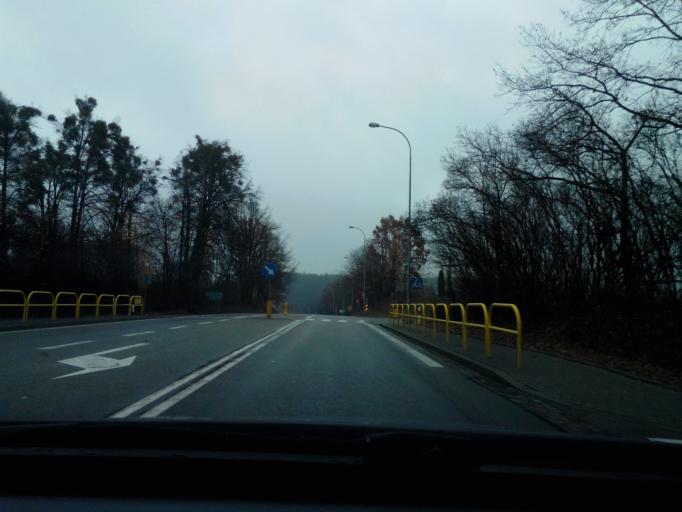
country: PL
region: Pomeranian Voivodeship
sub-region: Powiat starogardzki
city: Smetowo Graniczne
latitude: 53.7488
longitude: 18.7543
